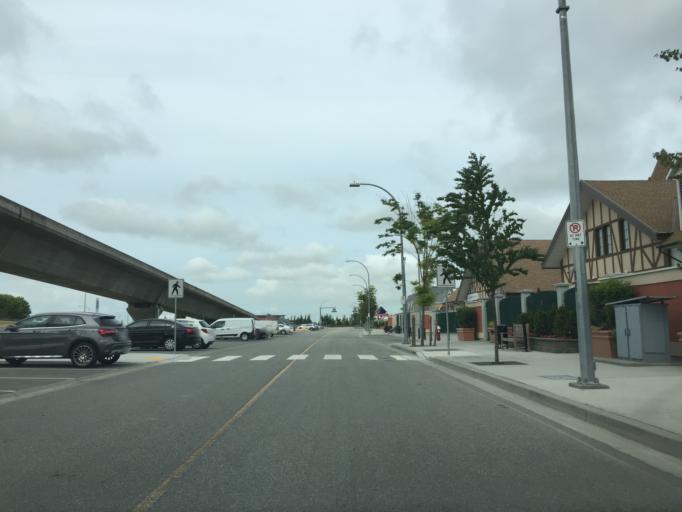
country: CA
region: British Columbia
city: Richmond
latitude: 49.1964
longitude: -123.1393
